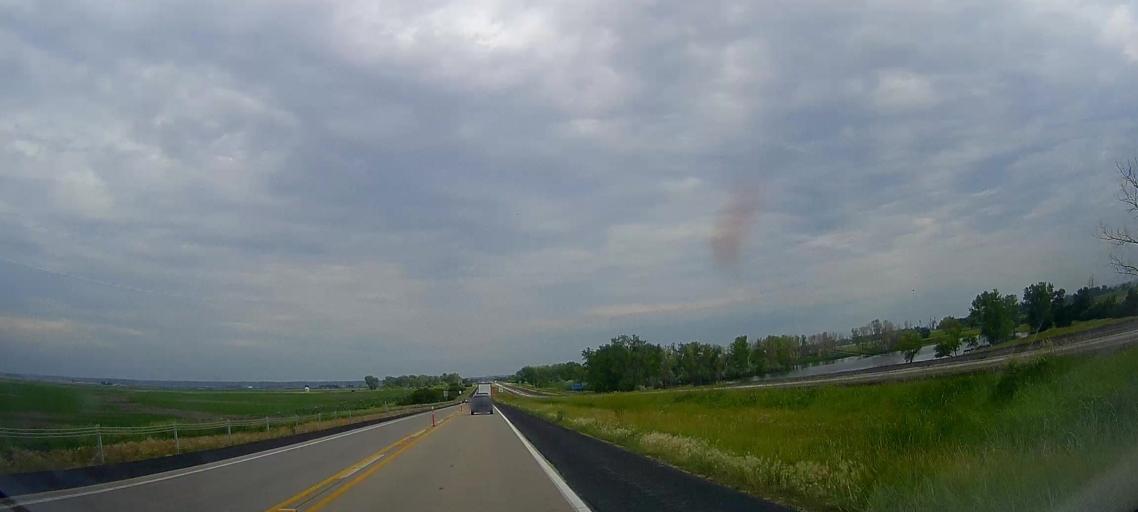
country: US
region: Nebraska
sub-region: Washington County
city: Blair
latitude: 41.6387
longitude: -96.0115
